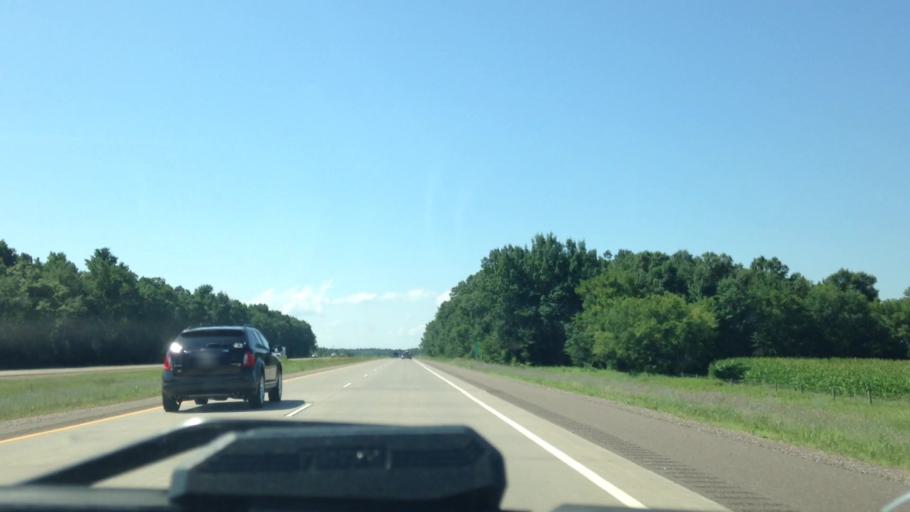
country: US
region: Wisconsin
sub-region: Barron County
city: Cameron
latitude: 45.4313
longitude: -91.7619
